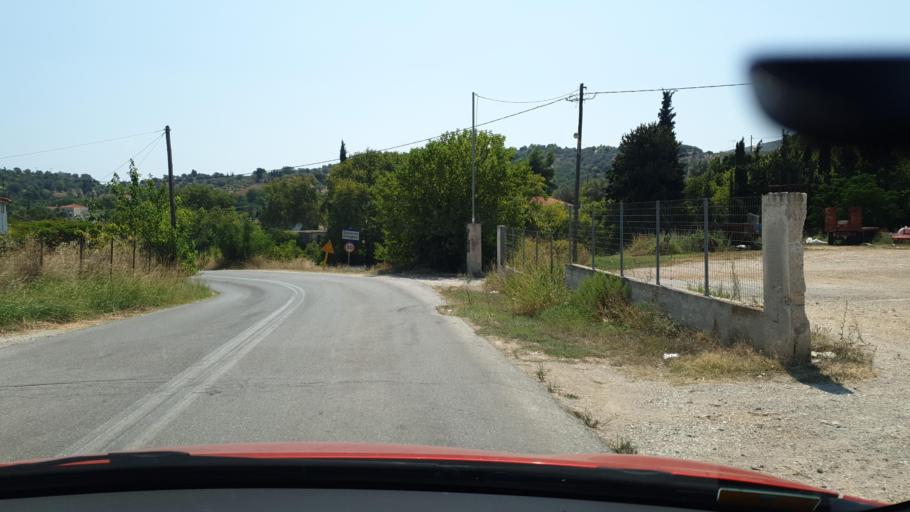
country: GR
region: Central Greece
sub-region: Nomos Evvoias
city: Oxilithos
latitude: 38.5295
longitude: 24.0867
